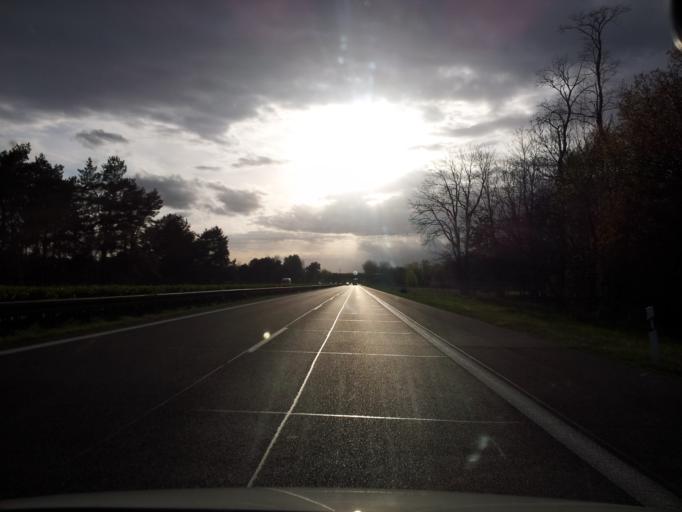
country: DE
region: Brandenburg
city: Lubbenau
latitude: 51.8399
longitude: 13.9486
